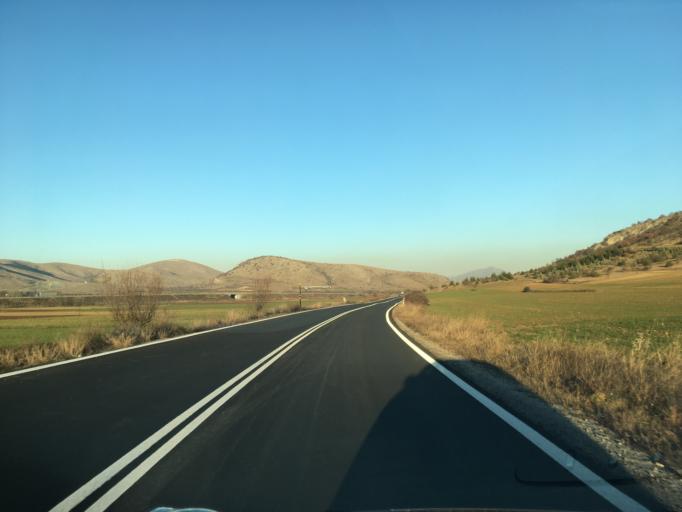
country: GR
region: West Macedonia
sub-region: Nomos Kozanis
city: Kozani
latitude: 40.3146
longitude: 21.7344
